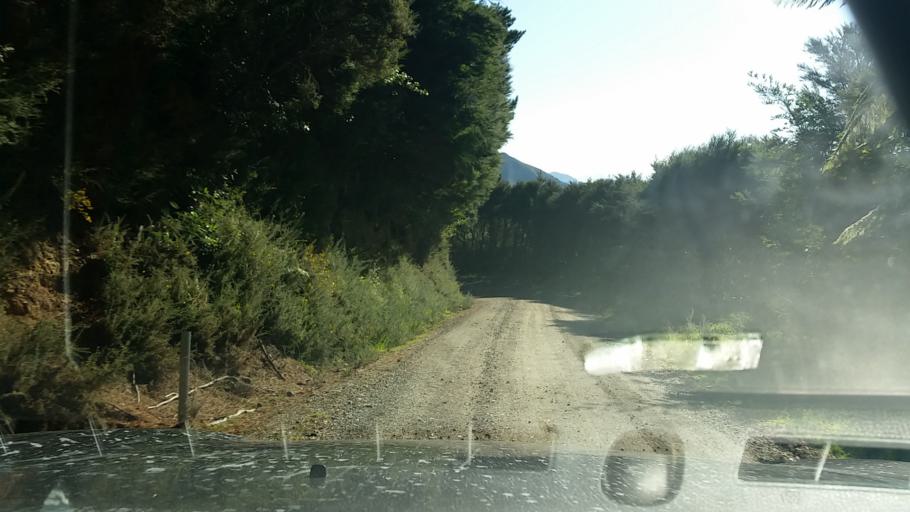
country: NZ
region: Marlborough
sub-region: Marlborough District
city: Picton
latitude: -41.1338
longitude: 174.0458
